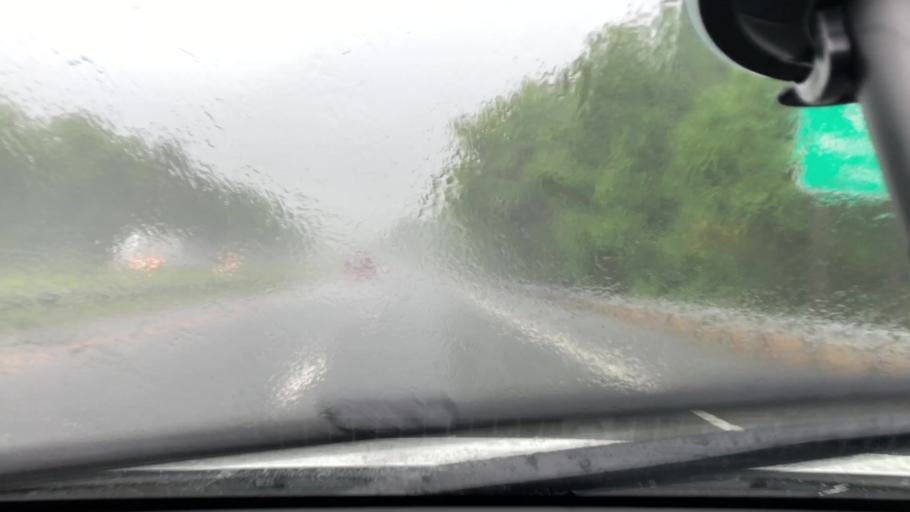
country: US
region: North Carolina
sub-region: Halifax County
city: Halifax
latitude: 36.3495
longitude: -77.6830
